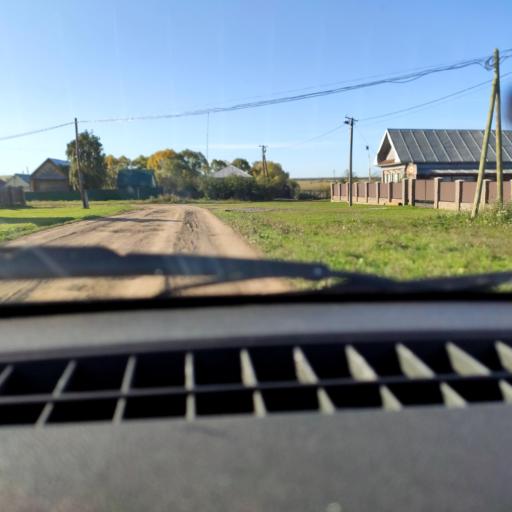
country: RU
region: Bashkortostan
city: Avdon
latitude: 54.5075
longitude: 55.7712
